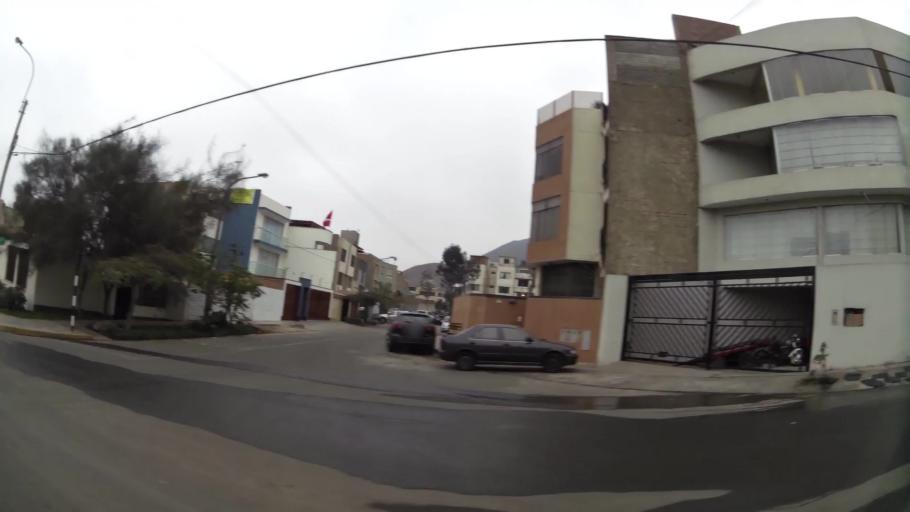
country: PE
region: Lima
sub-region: Lima
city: La Molina
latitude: -12.1139
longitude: -76.9374
